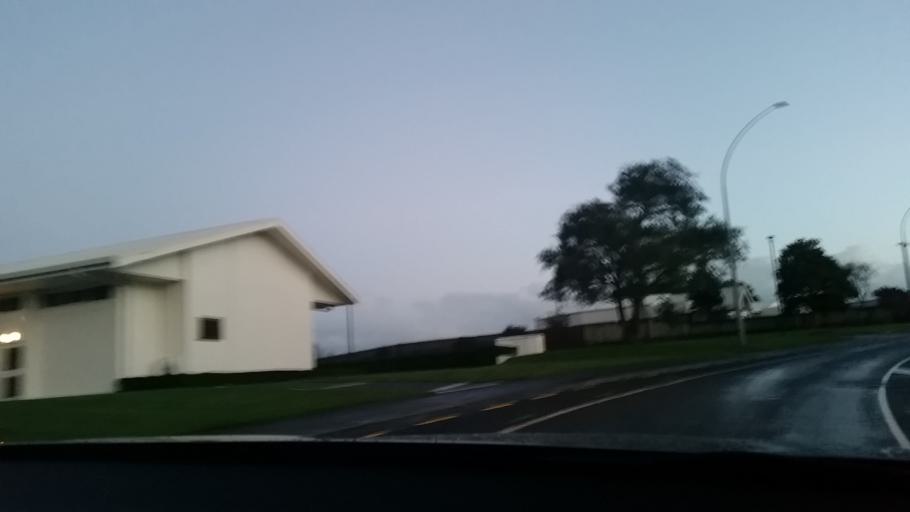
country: NZ
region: Waikato
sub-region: Hamilton City
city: Hamilton
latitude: -37.7994
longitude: 175.2481
